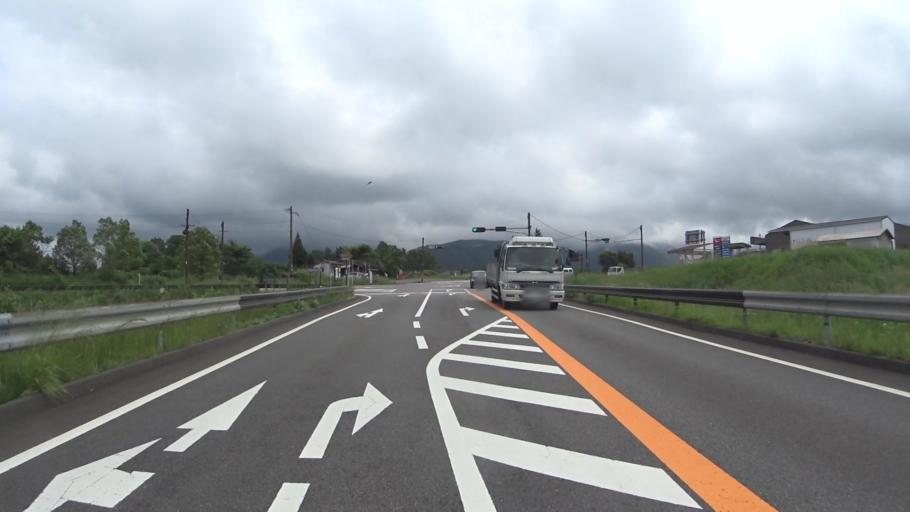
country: JP
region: Oita
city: Tsukawaki
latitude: 33.1579
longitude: 131.2408
